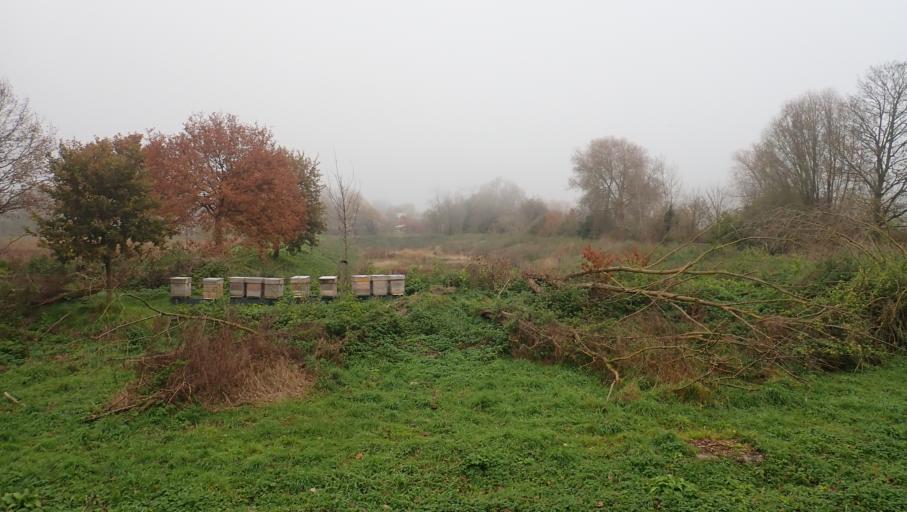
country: BE
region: Flanders
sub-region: Provincie Oost-Vlaanderen
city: Temse
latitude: 51.1221
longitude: 4.2285
